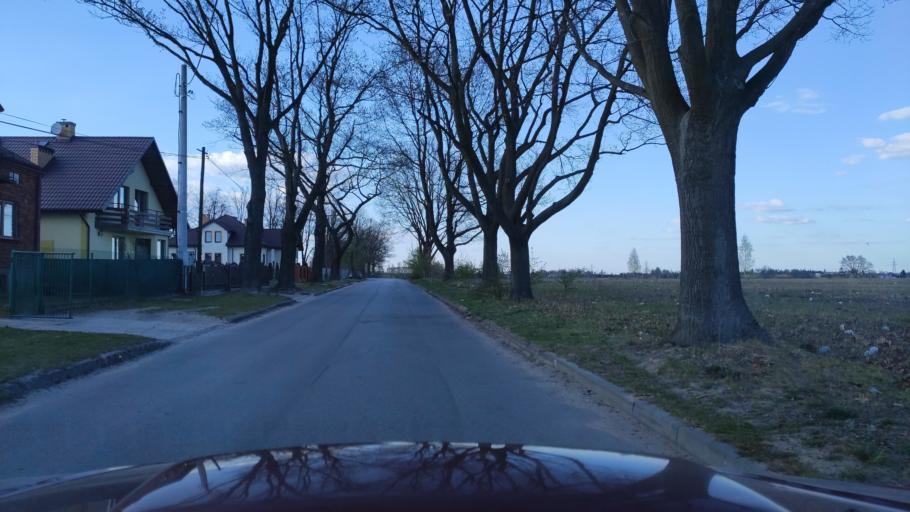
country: PL
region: Masovian Voivodeship
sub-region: Powiat zwolenski
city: Zwolen
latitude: 51.3620
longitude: 21.5759
